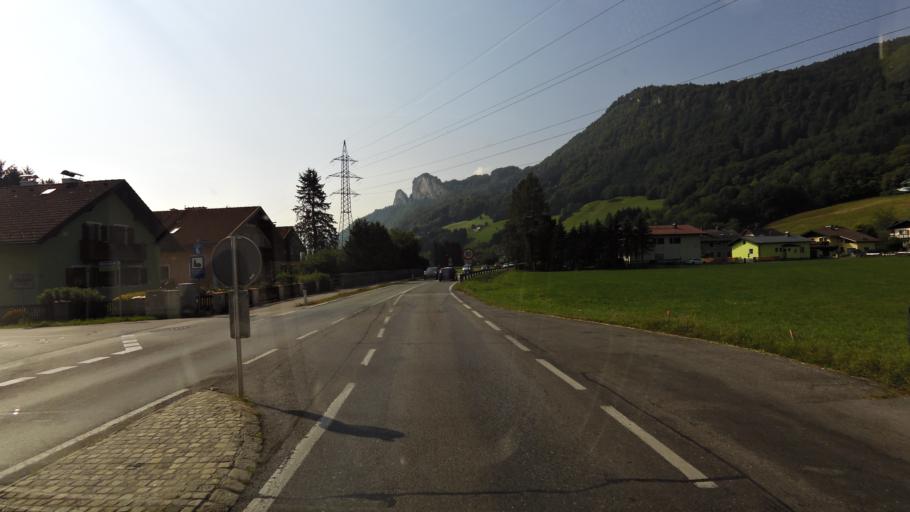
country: AT
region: Salzburg
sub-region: Politischer Bezirk Hallein
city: Puch bei Hallein
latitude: 47.7091
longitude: 13.0677
